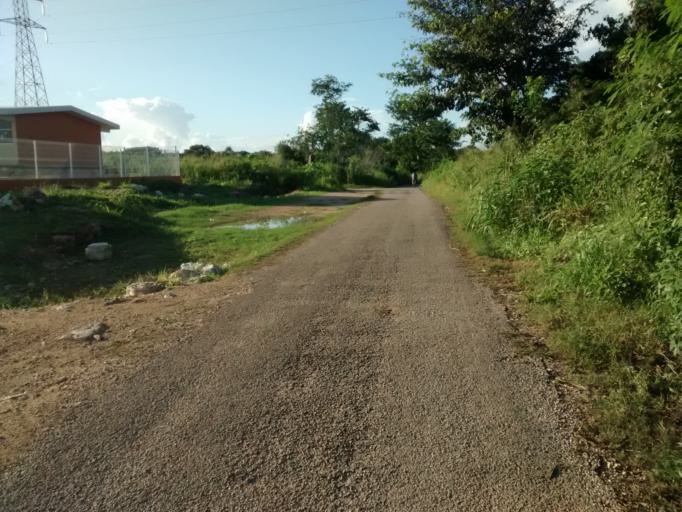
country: MX
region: Yucatan
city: Valladolid
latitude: 20.7089
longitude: -88.2158
